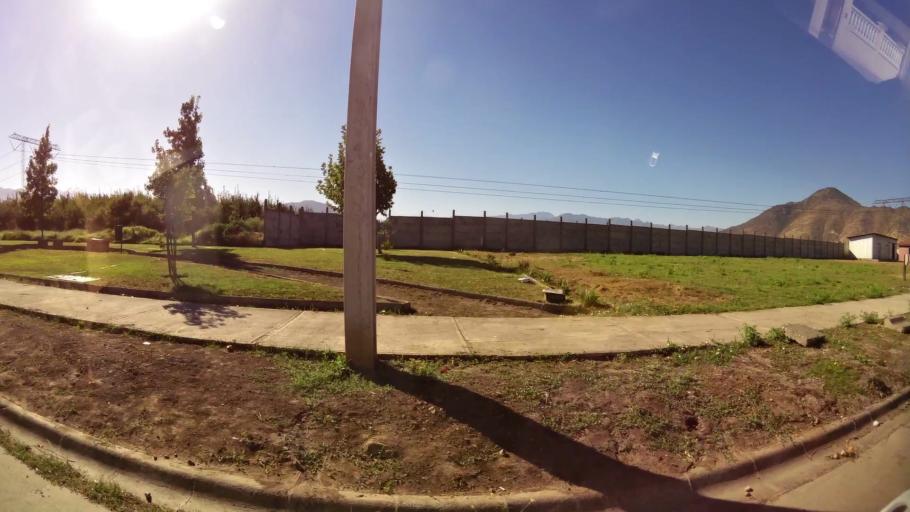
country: CL
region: O'Higgins
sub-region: Provincia de Cachapoal
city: Rancagua
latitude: -34.1958
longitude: -70.7187
